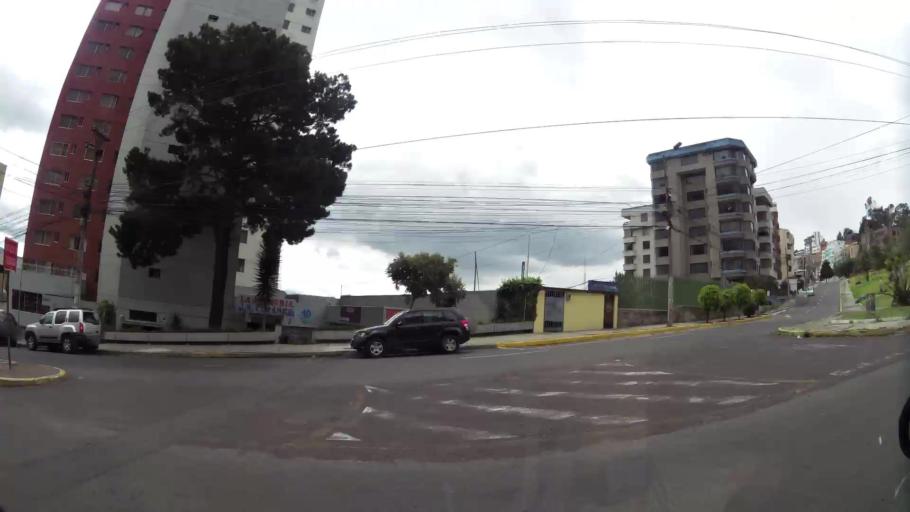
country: EC
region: Pichincha
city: Quito
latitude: -0.1718
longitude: -78.4720
